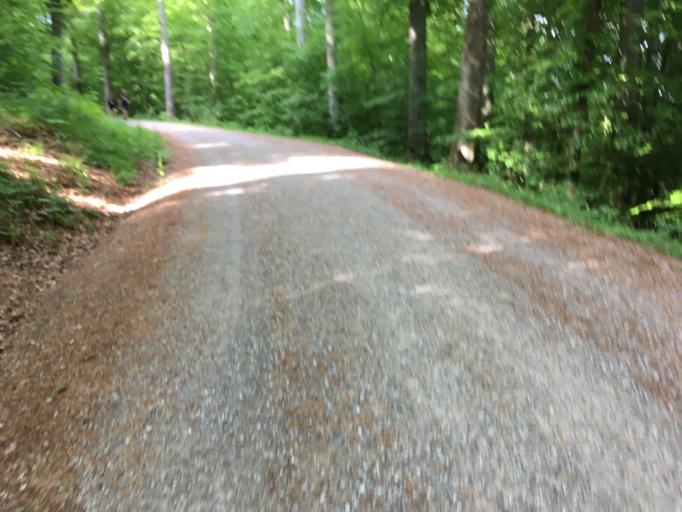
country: CH
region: Zurich
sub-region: Bezirk Zuerich
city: Zuerich (Kreis 7) / Fluntern
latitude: 47.3842
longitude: 8.5696
